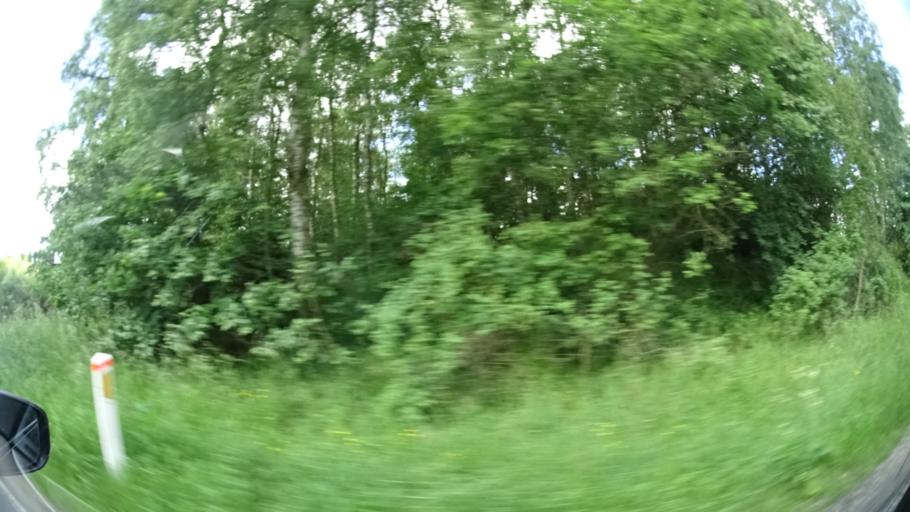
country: DK
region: Central Jutland
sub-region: Syddjurs Kommune
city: Ebeltoft
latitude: 56.2729
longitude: 10.6043
